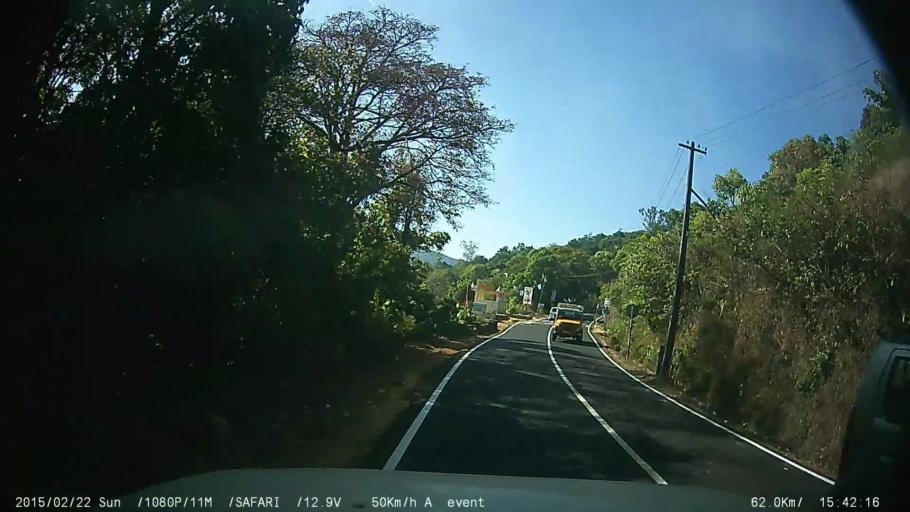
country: IN
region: Kerala
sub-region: Kottayam
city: Erattupetta
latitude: 9.5768
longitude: 76.9732
